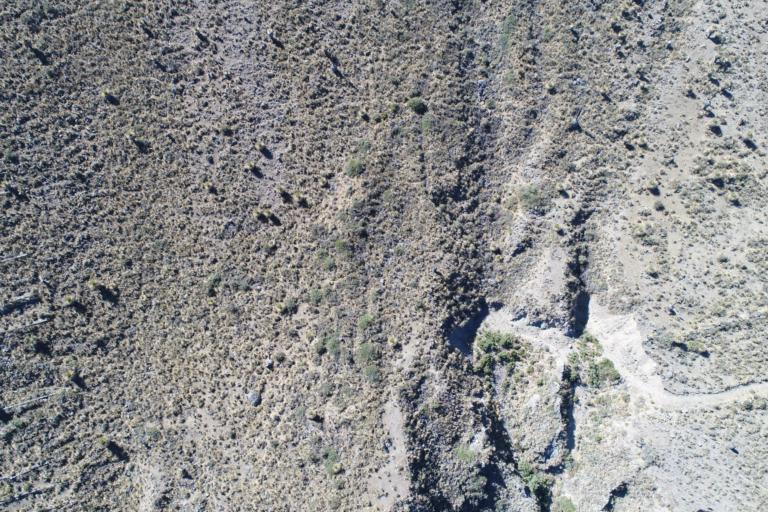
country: BO
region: La Paz
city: Viloco
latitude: -16.8147
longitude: -67.5557
